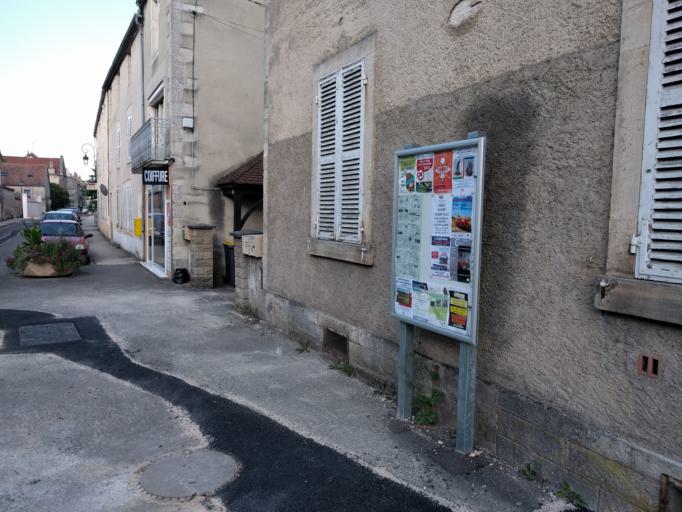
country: FR
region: Bourgogne
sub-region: Departement de la Cote-d'Or
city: Is-sur-Tille
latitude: 47.5207
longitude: 5.1091
